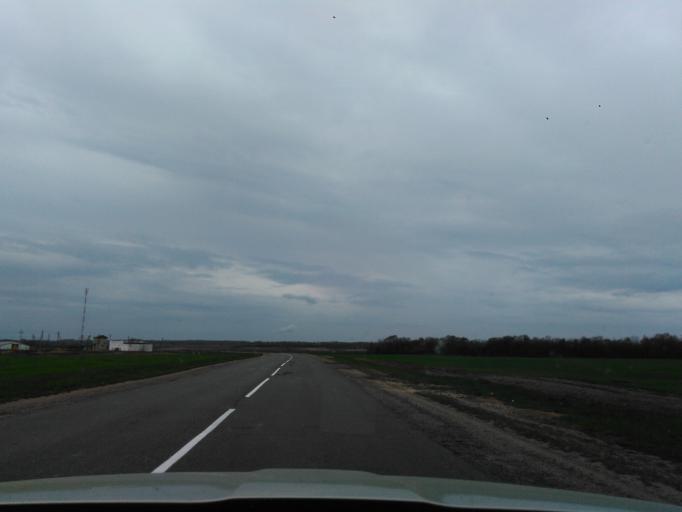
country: BY
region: Vitebsk
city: Chashniki
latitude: 54.7999
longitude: 29.1379
